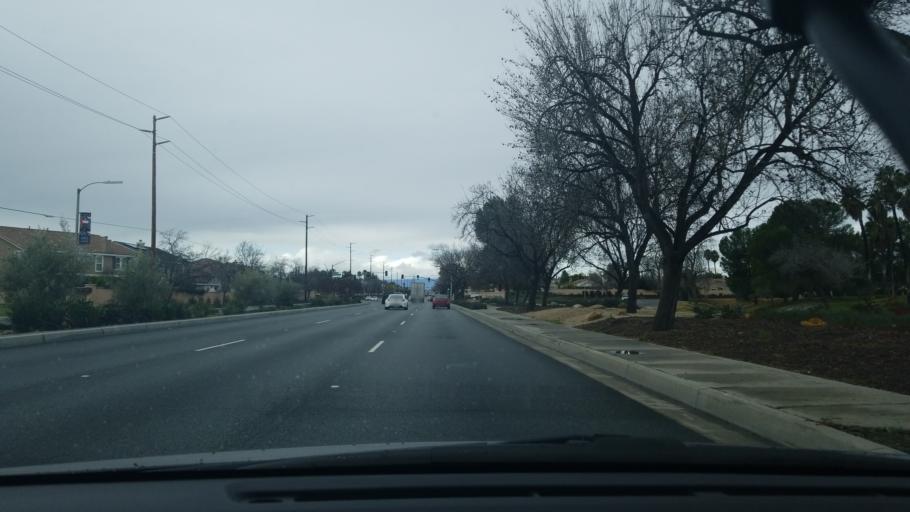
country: US
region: California
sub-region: Riverside County
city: Menifee
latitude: 33.6852
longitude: -117.1567
